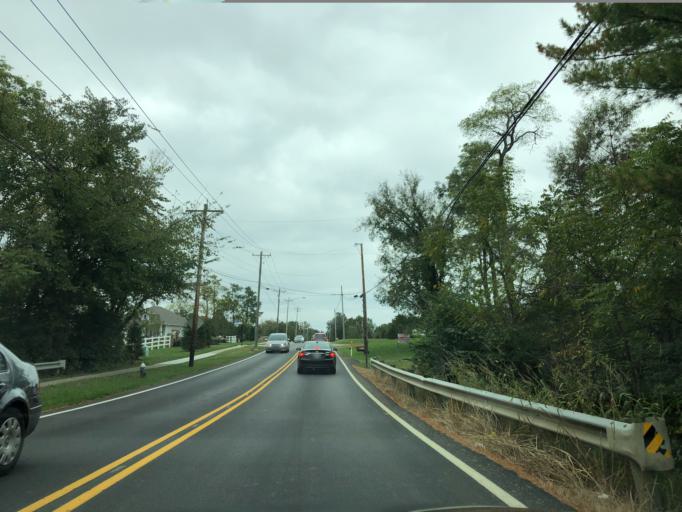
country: US
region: Ohio
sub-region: Hamilton County
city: Loveland
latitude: 39.2790
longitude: -84.2844
